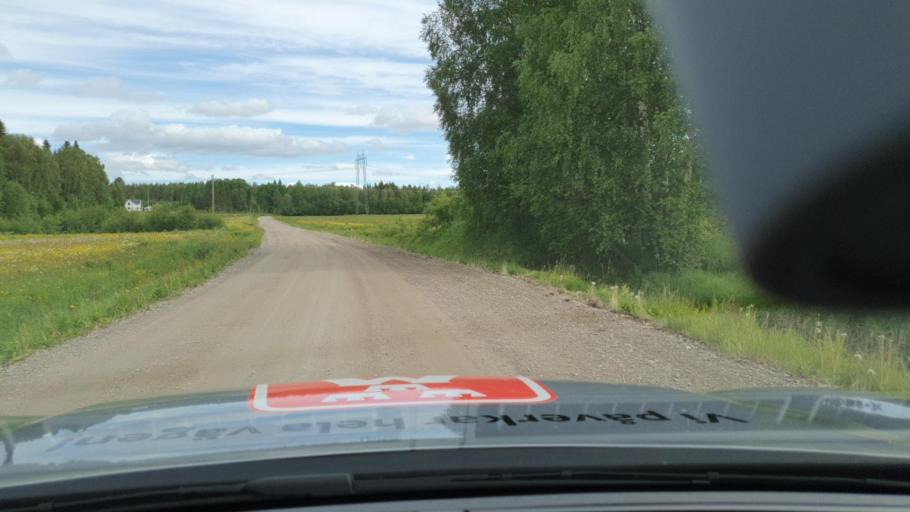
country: SE
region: Norrbotten
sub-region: Kalix Kommun
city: Rolfs
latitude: 65.8825
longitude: 23.0812
